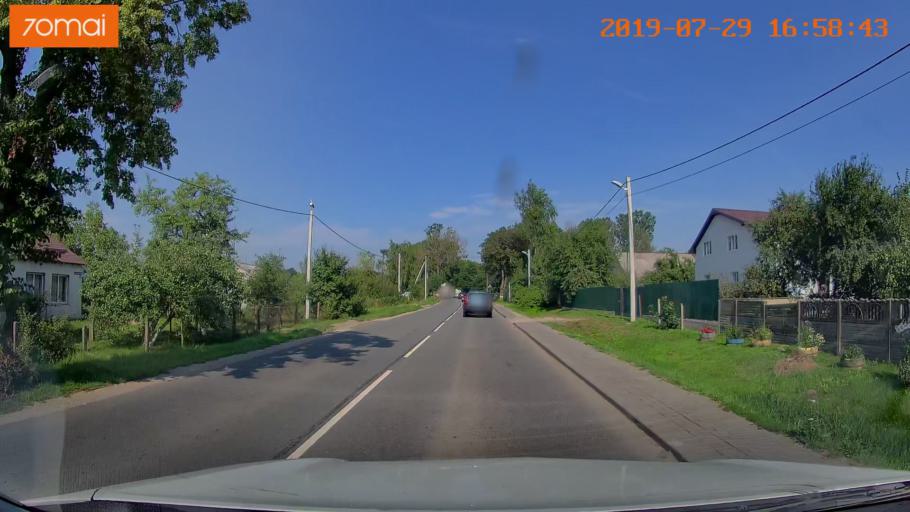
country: RU
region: Kaliningrad
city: Volochayevskoye
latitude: 54.8182
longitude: 20.2069
